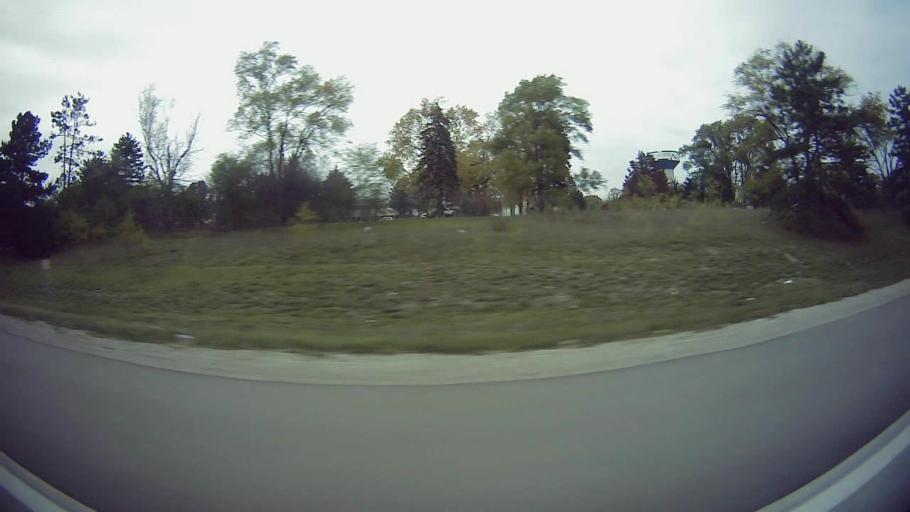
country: US
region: Michigan
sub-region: Oakland County
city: Farmington Hills
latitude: 42.4899
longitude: -83.4226
